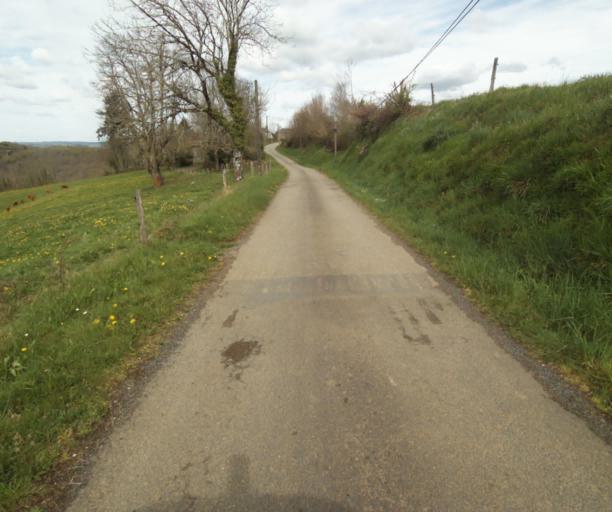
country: FR
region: Limousin
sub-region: Departement de la Correze
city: Laguenne
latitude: 45.2230
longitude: 1.8480
